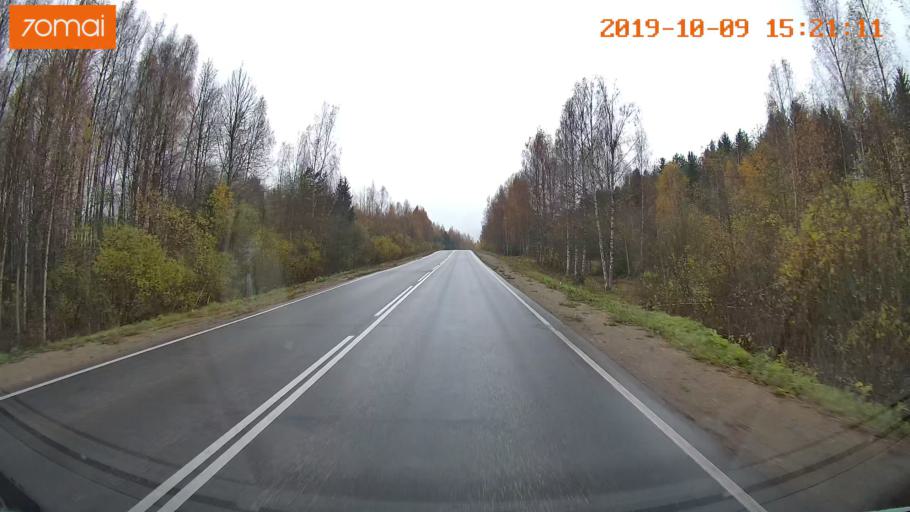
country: RU
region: Kostroma
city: Susanino
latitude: 58.0561
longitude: 41.5243
